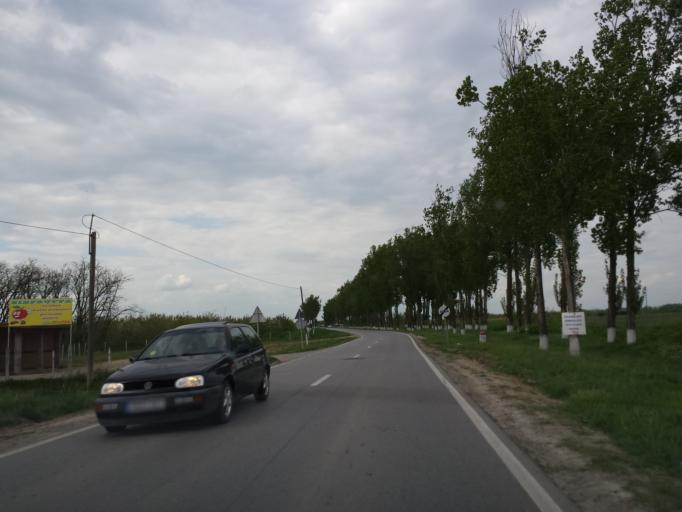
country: RO
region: Timis
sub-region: Comuna Cenad
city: Cenad
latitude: 46.1179
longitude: 20.5961
